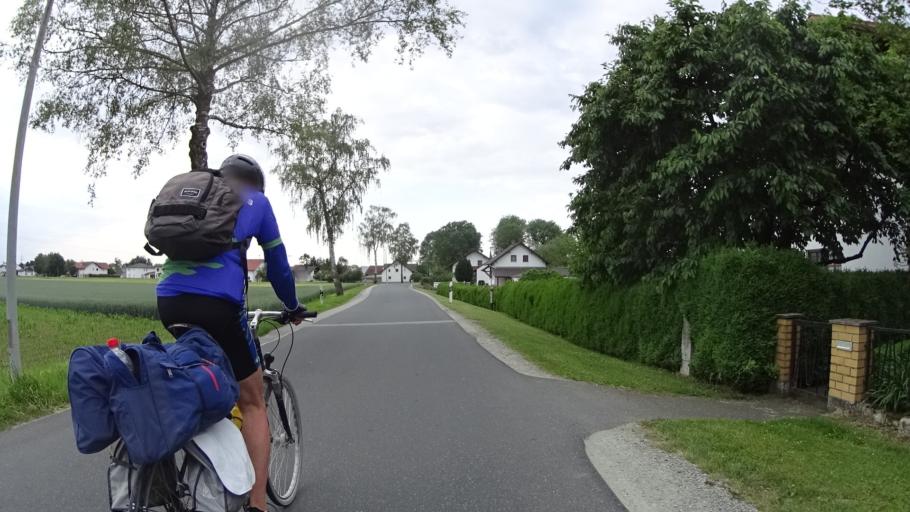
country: DE
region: Bavaria
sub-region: Lower Bavaria
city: Parkstetten
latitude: 48.9122
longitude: 12.6236
